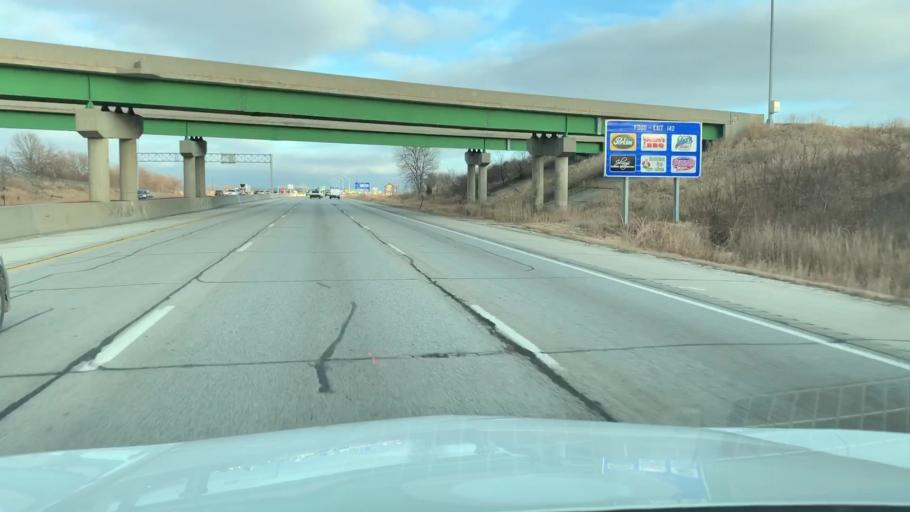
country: US
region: Iowa
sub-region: Polk County
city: Altoona
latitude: 41.6599
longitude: -93.5221
